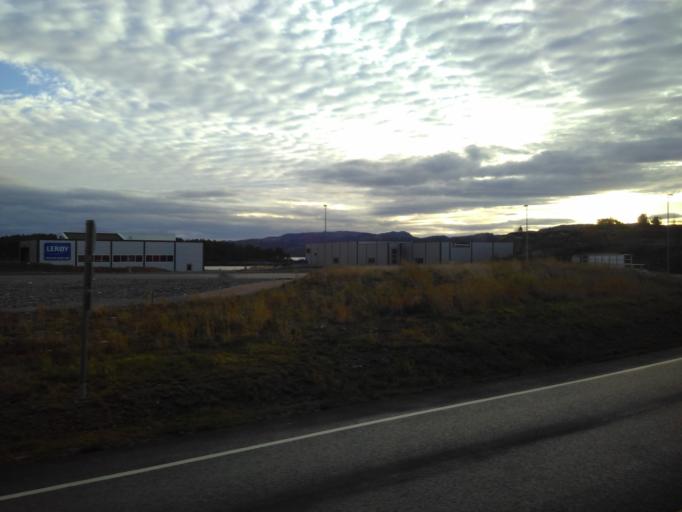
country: NO
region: Sor-Trondelag
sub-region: Hitra
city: Fillan
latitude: 63.5196
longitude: 9.1098
